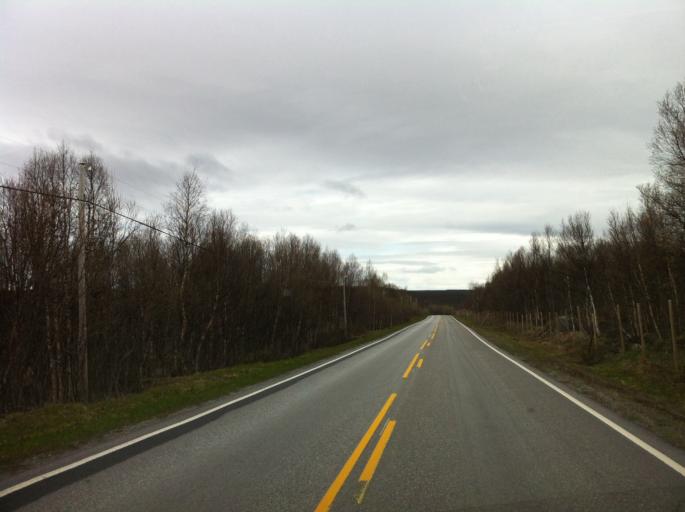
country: NO
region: Sor-Trondelag
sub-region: Tydal
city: Aas
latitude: 62.6379
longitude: 11.9074
